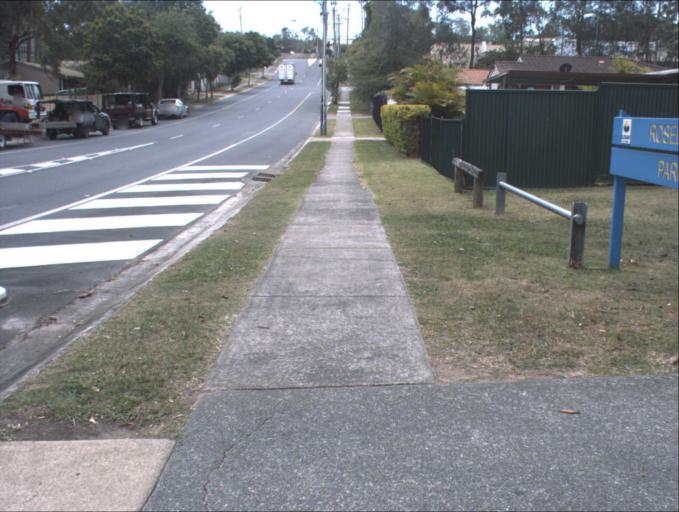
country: AU
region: Queensland
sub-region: Logan
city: Slacks Creek
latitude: -27.6457
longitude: 153.1740
